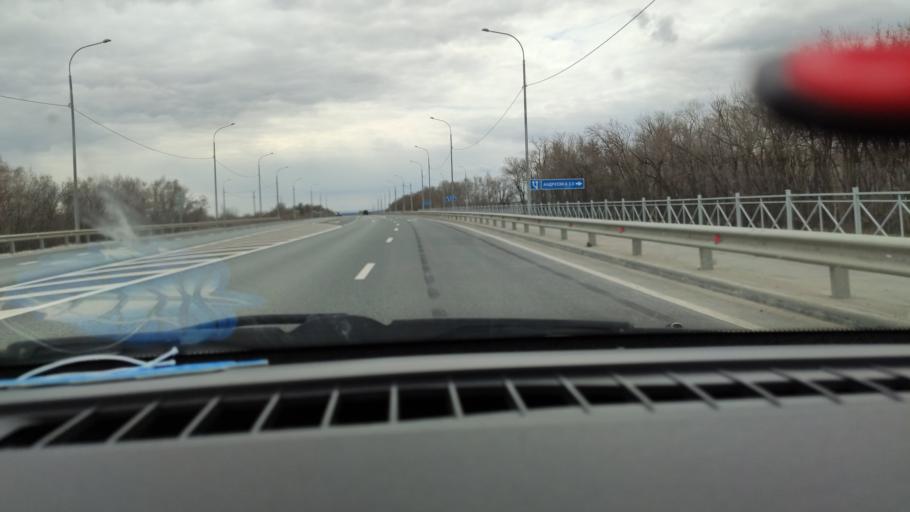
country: RU
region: Saratov
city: Yelshanka
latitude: 51.8906
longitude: 46.5231
